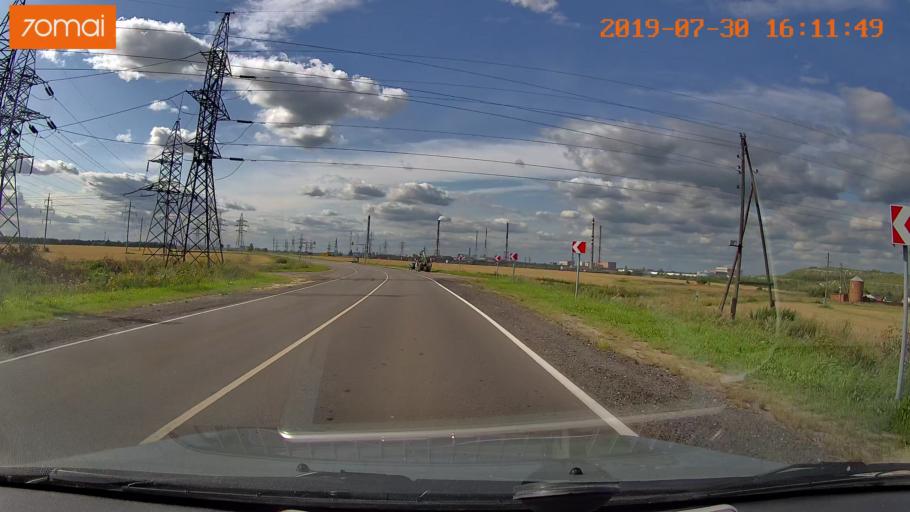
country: RU
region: Moskovskaya
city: Lopatinskiy
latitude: 55.2814
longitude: 38.7070
